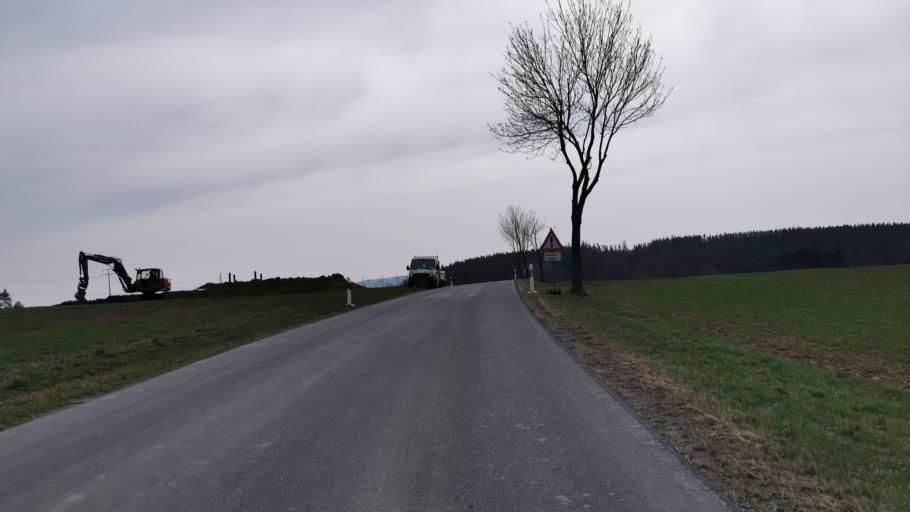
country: DE
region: Thuringia
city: Leutenberg
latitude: 50.5339
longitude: 11.4319
